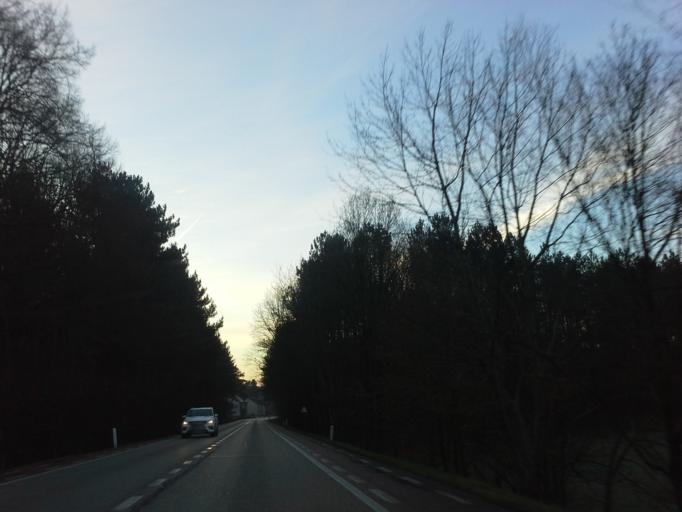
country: BE
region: Flanders
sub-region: Provincie Limburg
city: Tessenderlo
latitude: 51.0405
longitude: 5.0527
